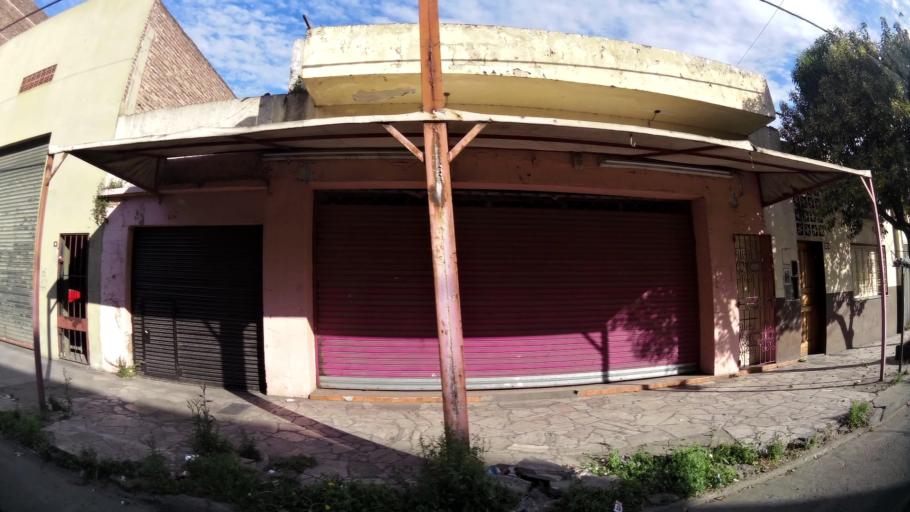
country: AR
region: Buenos Aires
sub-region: Partido de Avellaneda
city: Avellaneda
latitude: -34.6994
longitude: -58.3523
